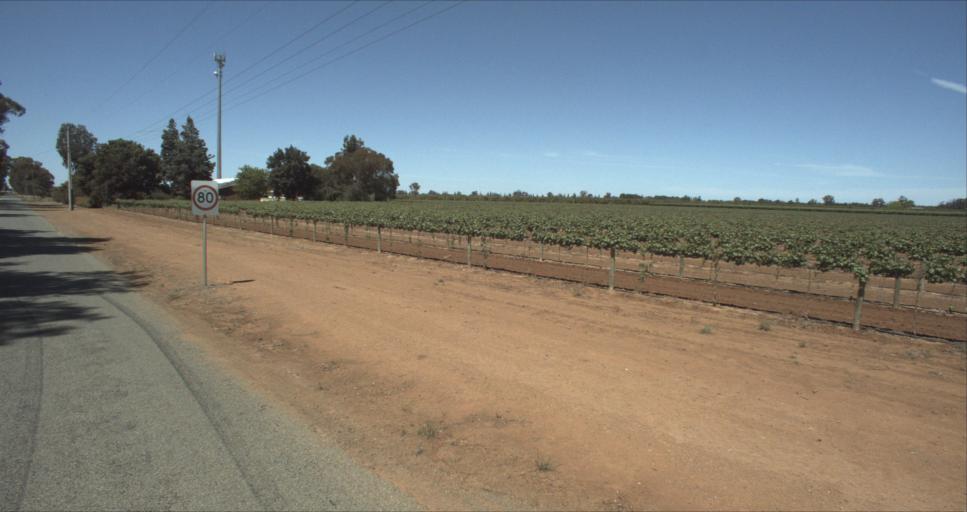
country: AU
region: New South Wales
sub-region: Leeton
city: Leeton
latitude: -34.5312
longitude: 146.3342
